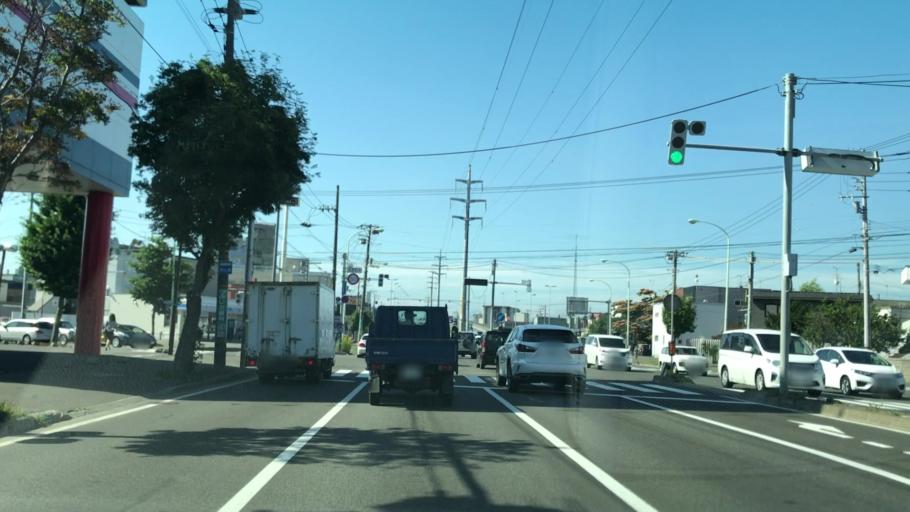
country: JP
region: Hokkaido
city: Sapporo
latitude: 43.0631
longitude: 141.4078
